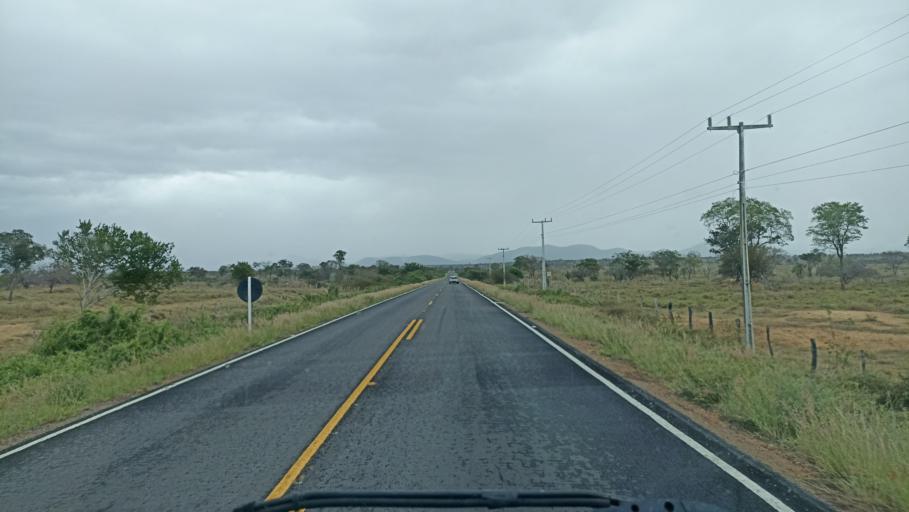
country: BR
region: Bahia
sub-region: Maracas
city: Maracas
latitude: -13.0379
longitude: -40.6964
